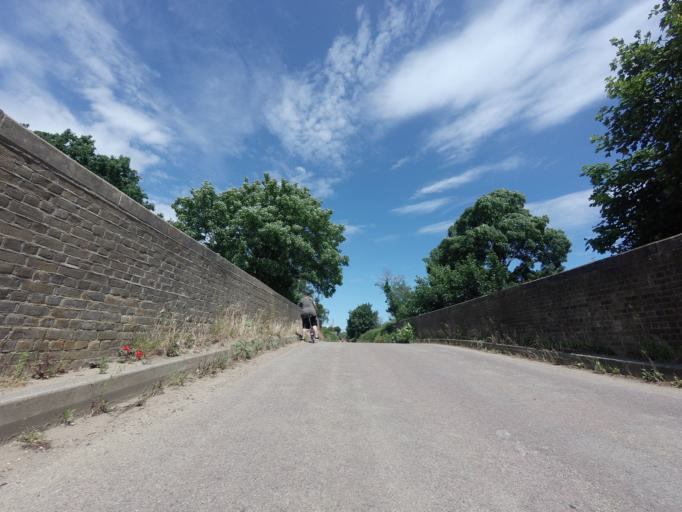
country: GB
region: England
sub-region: Kent
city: Cliffe
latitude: 51.4450
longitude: 0.4909
